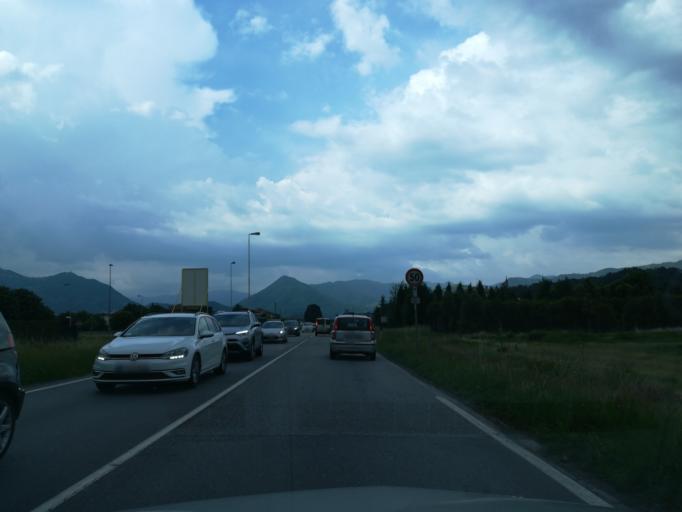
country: IT
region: Lombardy
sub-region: Provincia di Bergamo
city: Scano al Brembo
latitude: 45.7208
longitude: 9.6101
